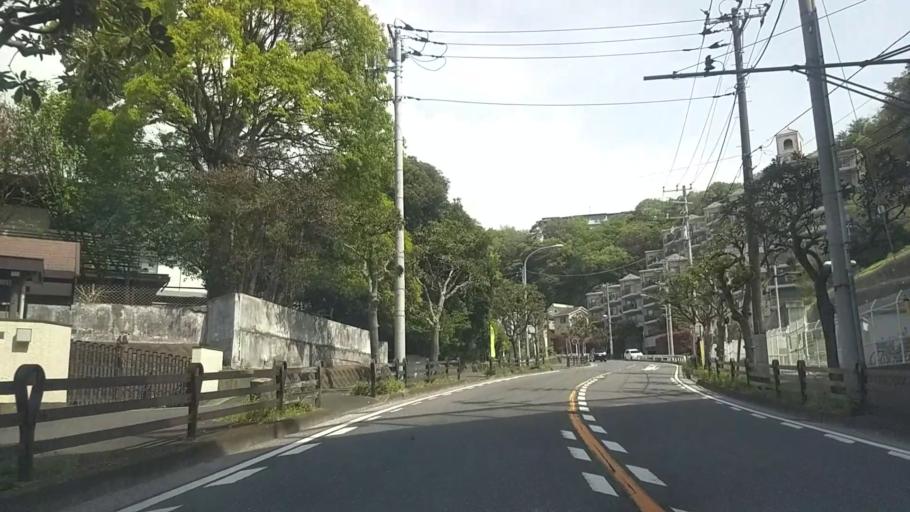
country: JP
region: Kanagawa
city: Yokohama
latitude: 35.3961
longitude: 139.6092
